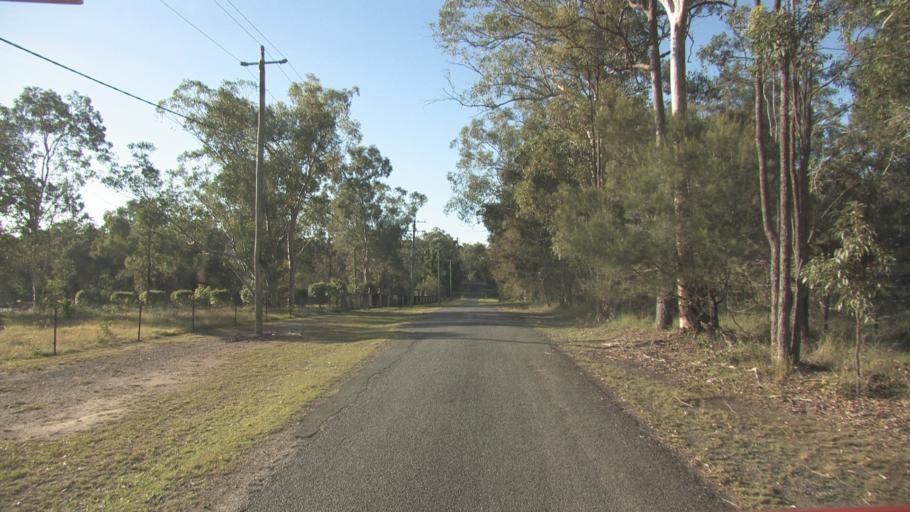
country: AU
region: Queensland
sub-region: Gold Coast
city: Yatala
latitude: -27.6650
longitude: 153.2451
